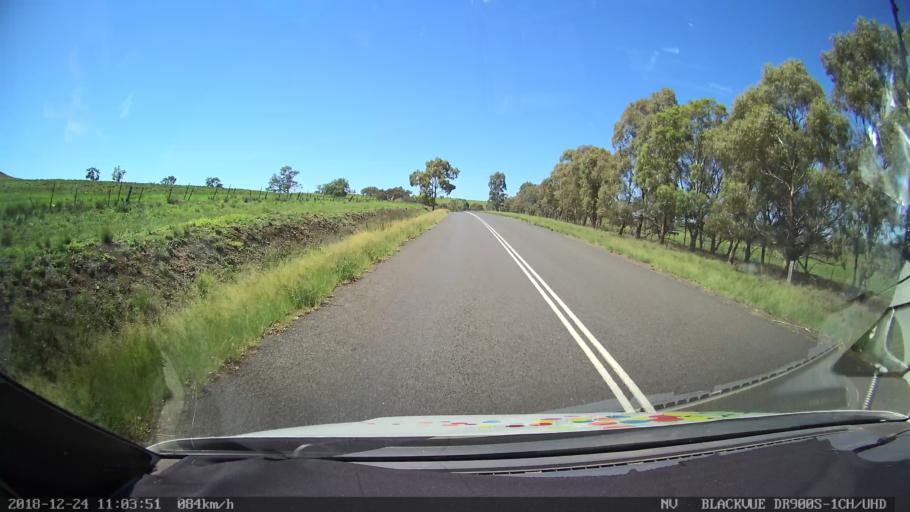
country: AU
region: New South Wales
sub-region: Upper Hunter Shire
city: Merriwa
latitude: -32.1020
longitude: 150.3690
